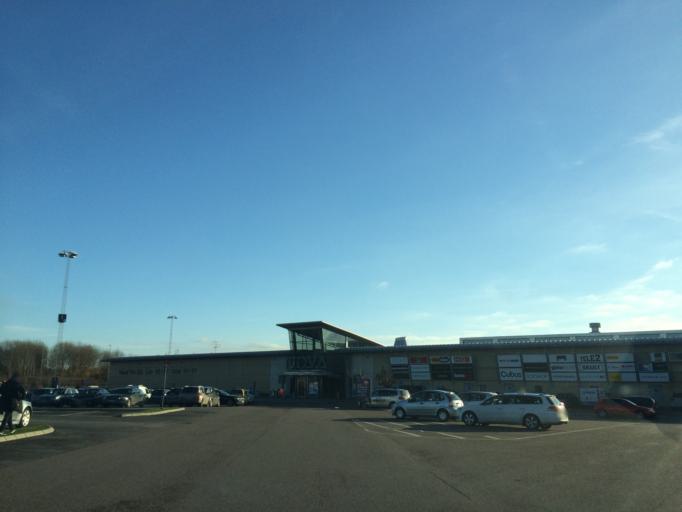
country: SE
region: Skane
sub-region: Lunds Kommun
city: Lund
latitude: 55.7151
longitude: 13.1587
